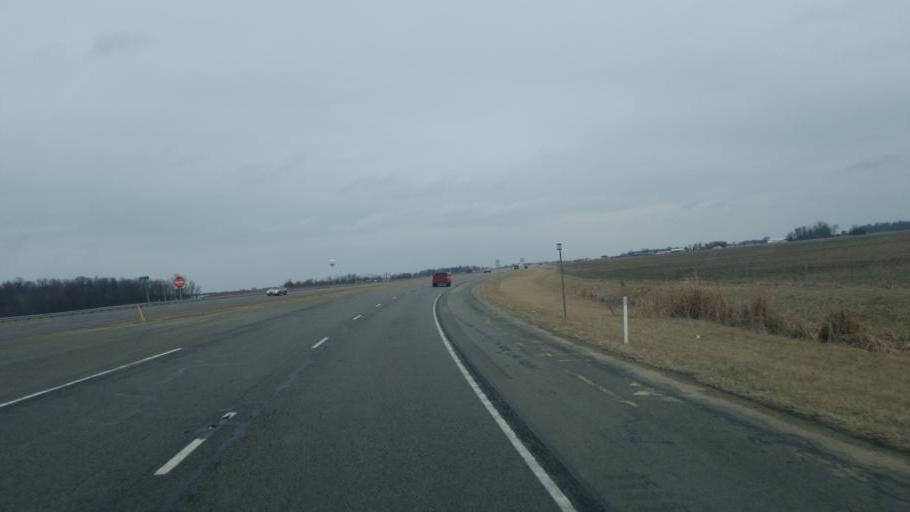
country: US
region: Indiana
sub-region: Adams County
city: Decatur
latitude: 40.7570
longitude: -84.9395
